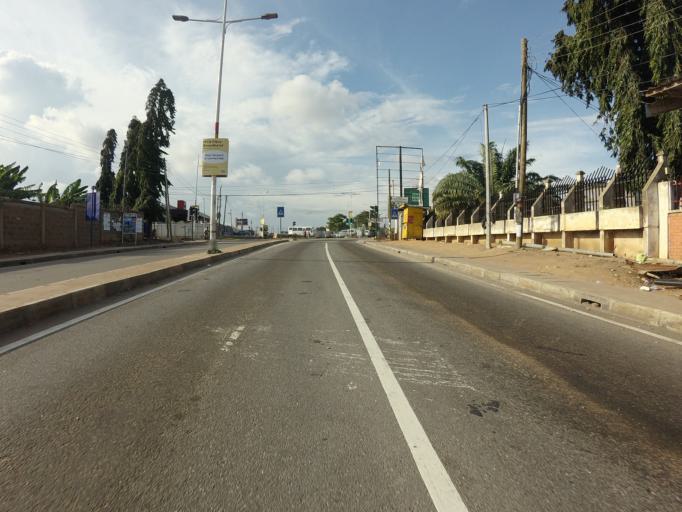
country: GH
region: Greater Accra
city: Medina Estates
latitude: 5.6241
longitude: -0.1529
